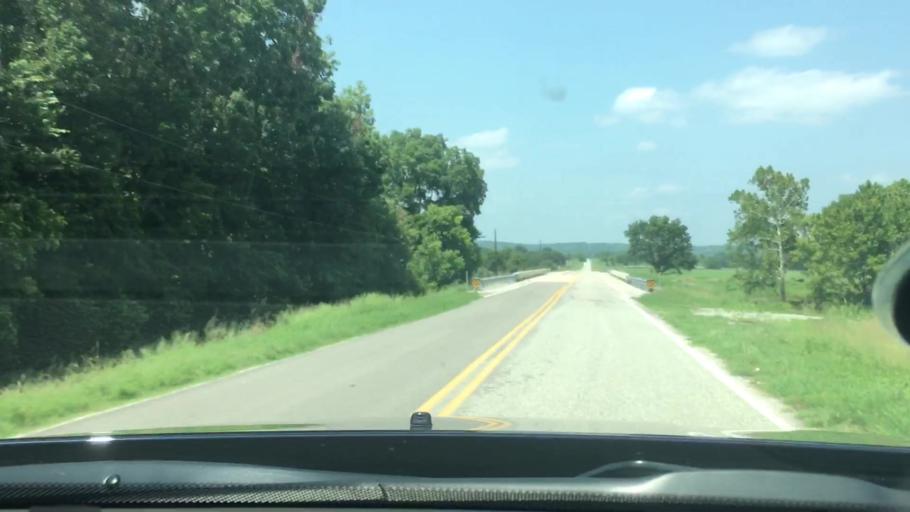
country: US
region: Oklahoma
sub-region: Johnston County
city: Tishomingo
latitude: 34.3885
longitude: -96.4962
